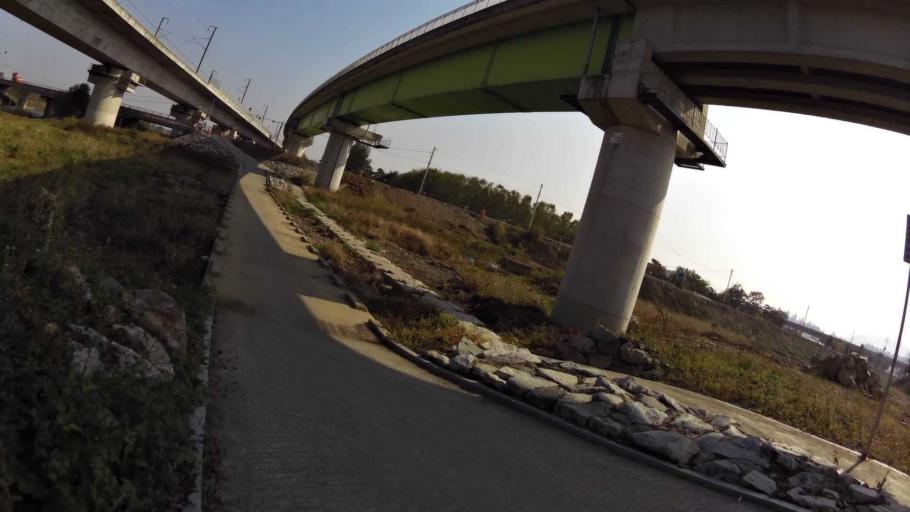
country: KR
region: Gyeongsangbuk-do
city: Gyeongsan-si
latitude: 35.8538
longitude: 128.7085
